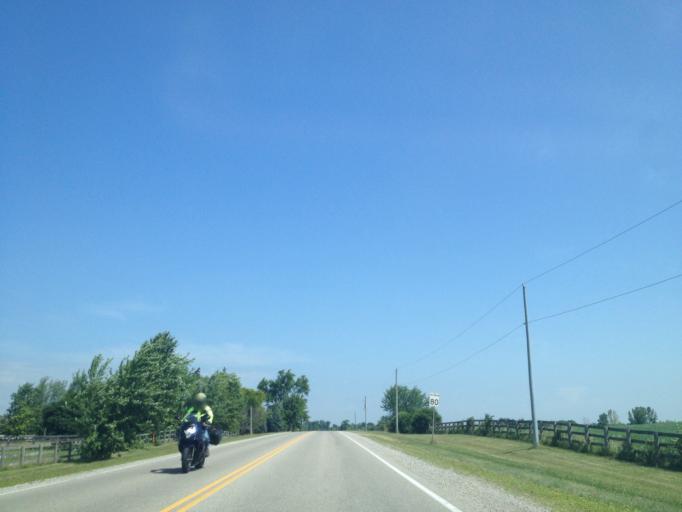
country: CA
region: Ontario
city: London
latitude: 43.2002
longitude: -81.2417
